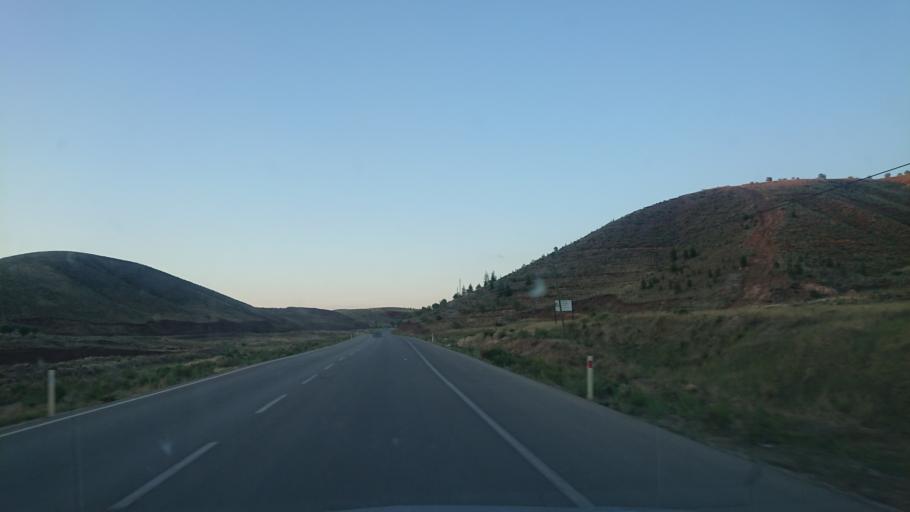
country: TR
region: Aksaray
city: Aksaray
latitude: 38.4200
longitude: 34.0217
